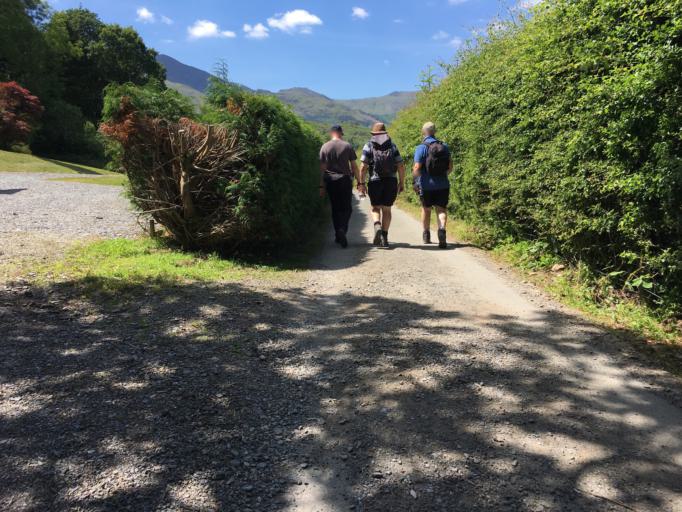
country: GB
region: Wales
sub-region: Gwynedd
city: Penrhyndeudraeth
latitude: 53.0165
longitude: -4.0889
